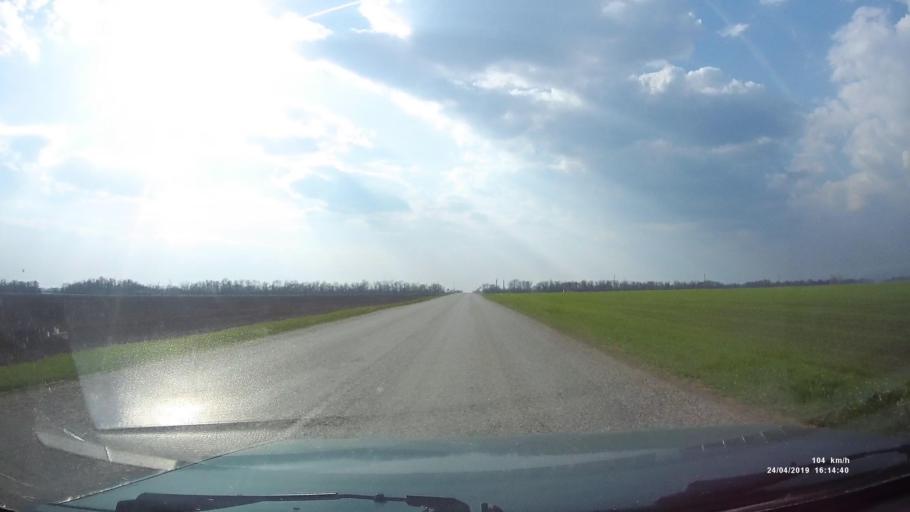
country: RU
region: Rostov
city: Sovetskoye
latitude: 46.7532
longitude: 42.1974
